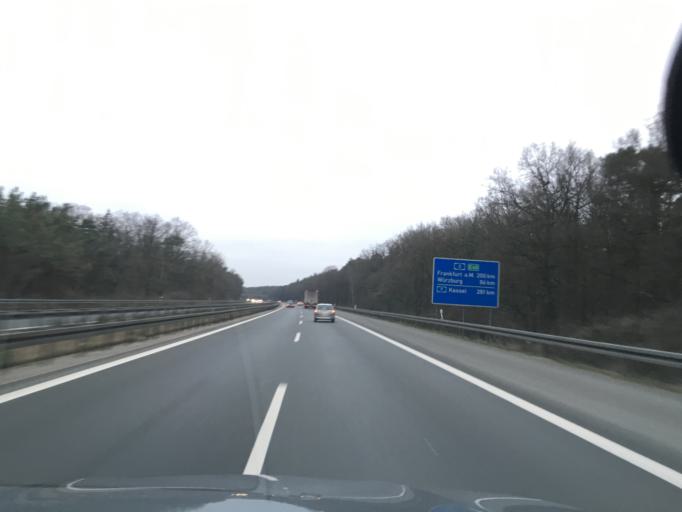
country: DE
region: Bavaria
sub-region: Regierungsbezirk Mittelfranken
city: Hessdorf
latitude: 49.6356
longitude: 10.9156
